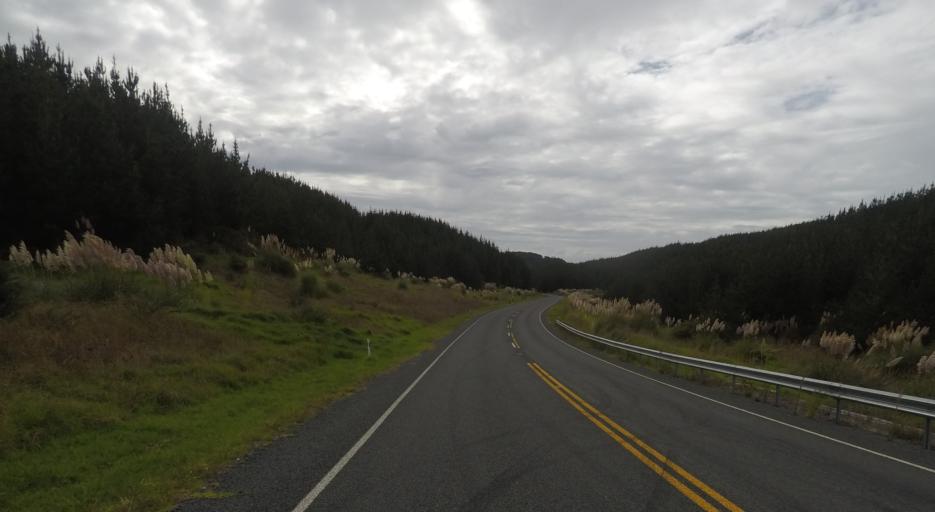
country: NZ
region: Auckland
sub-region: Auckland
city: Rothesay Bay
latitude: -36.6544
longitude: 174.7013
